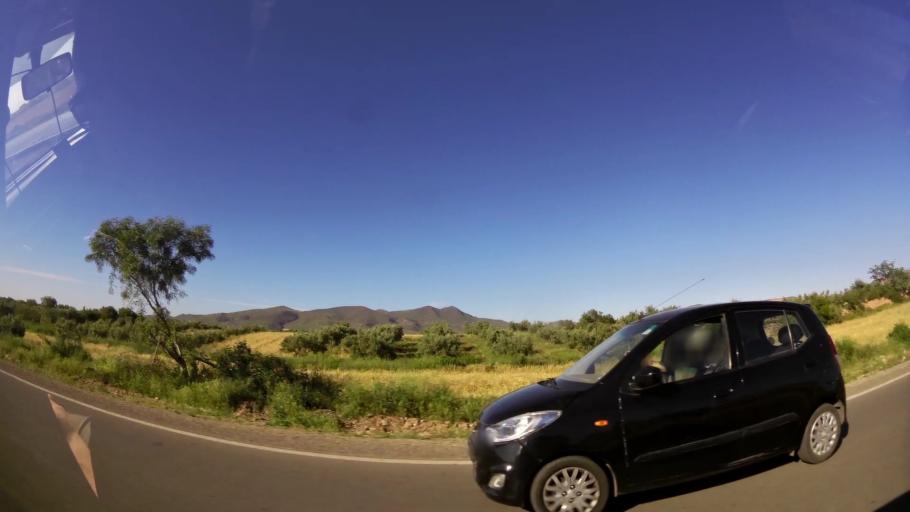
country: MA
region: Oriental
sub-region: Berkane-Taourirt
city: Ahfir
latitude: 34.9693
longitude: -2.1207
